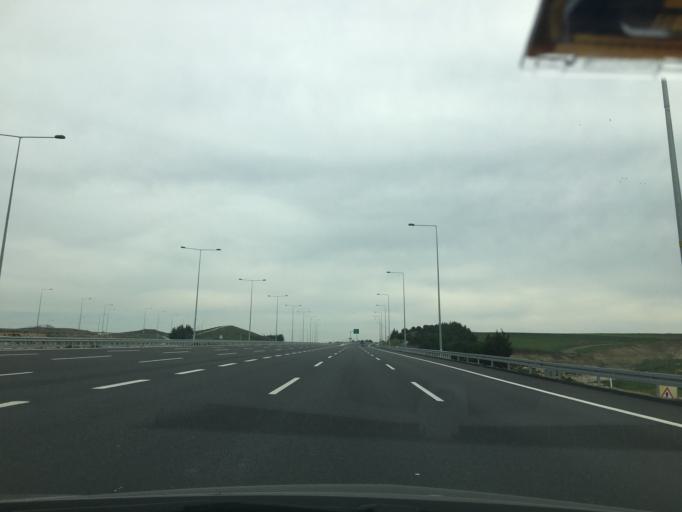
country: TR
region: Istanbul
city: Silivri
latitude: 41.1148
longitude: 28.1750
